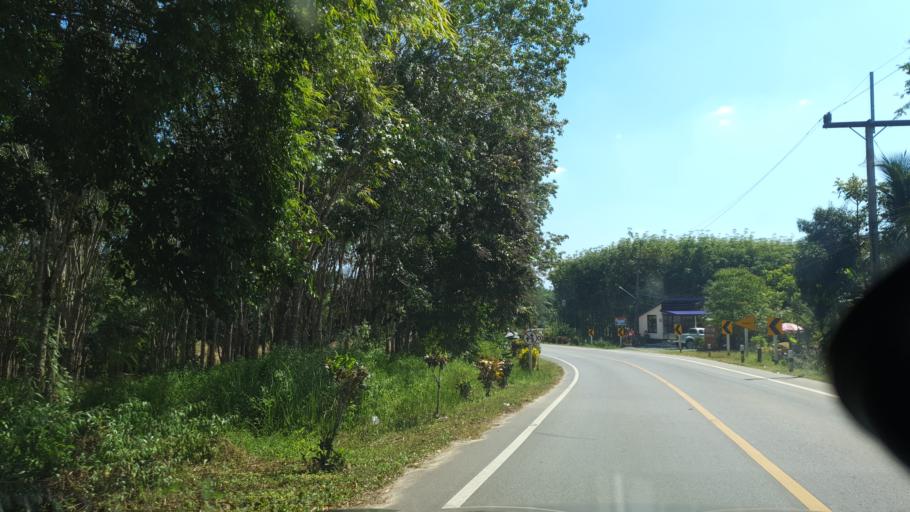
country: TH
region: Krabi
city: Khlong Thom
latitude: 7.9333
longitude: 99.2217
